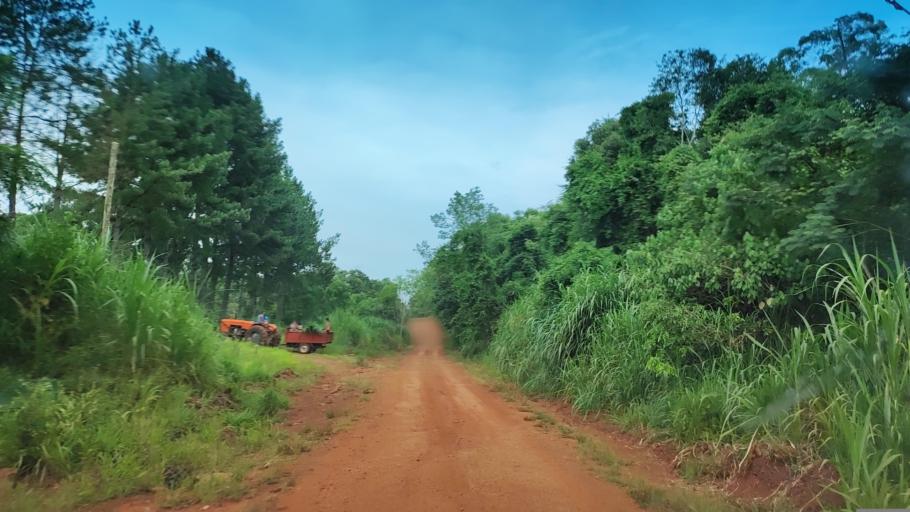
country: AR
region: Misiones
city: Gobernador Roca
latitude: -27.1480
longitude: -55.4797
